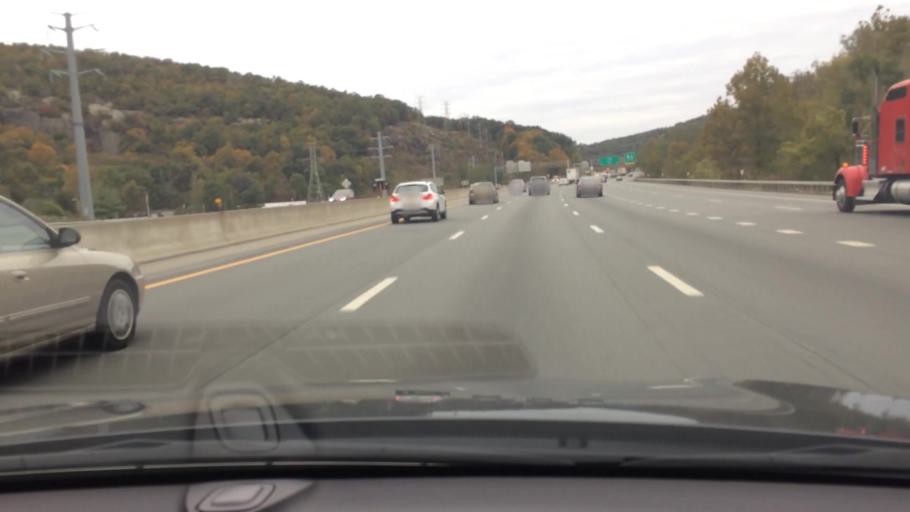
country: US
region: New York
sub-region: Rockland County
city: Suffern
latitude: 41.1297
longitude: -74.1674
